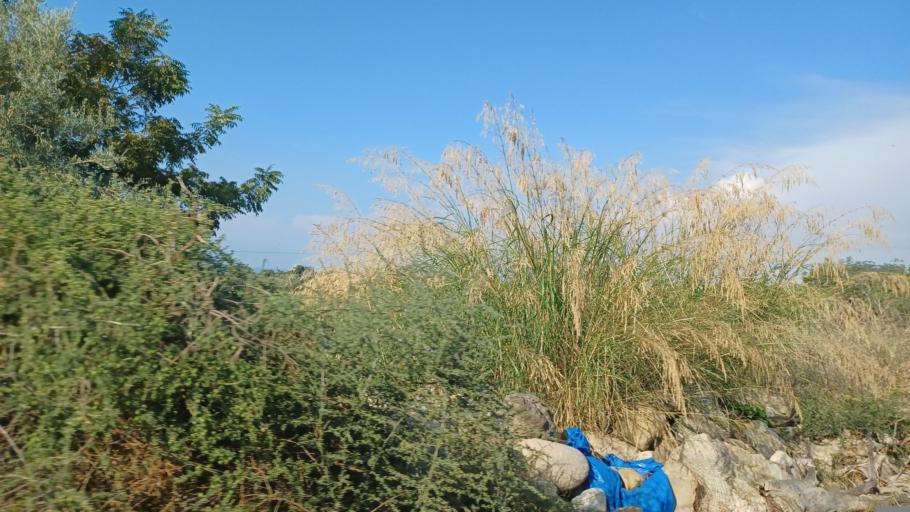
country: CY
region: Pafos
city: Kissonerga
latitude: 34.8432
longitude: 32.3923
